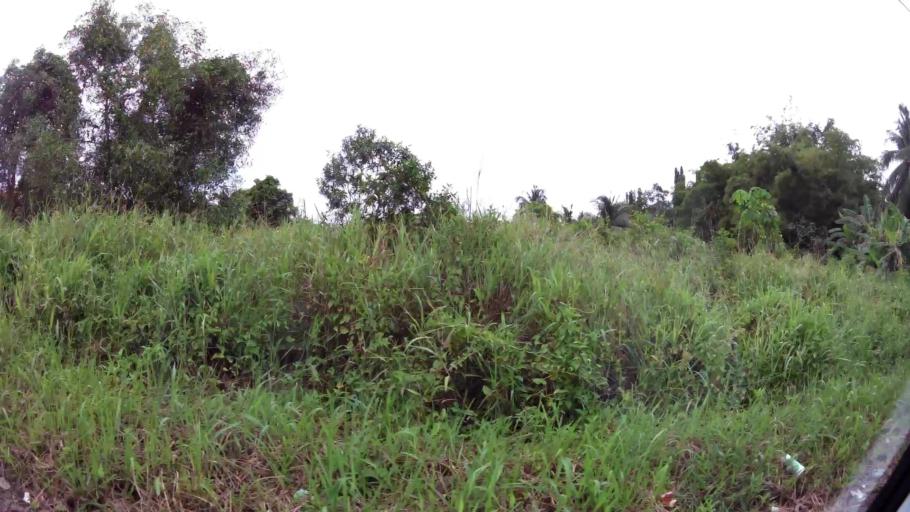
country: BN
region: Brunei and Muara
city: Bandar Seri Begawan
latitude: 4.8952
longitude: 114.9290
